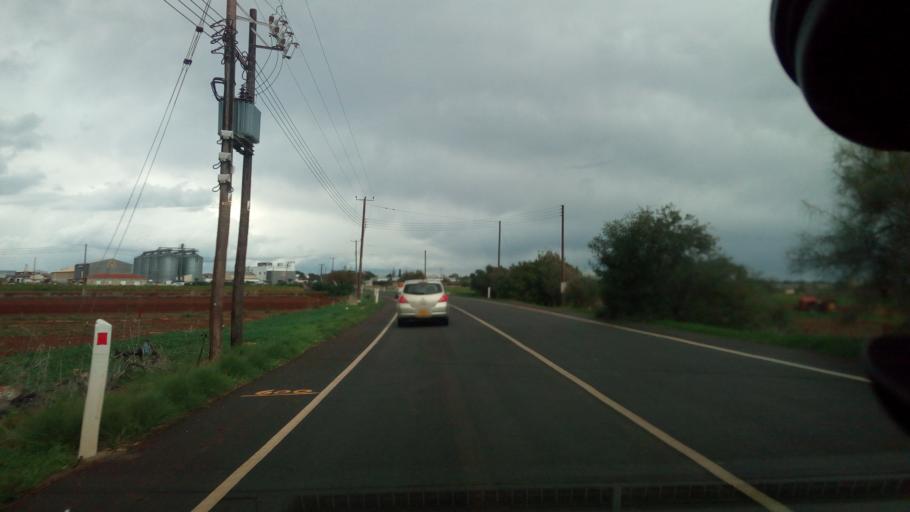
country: CY
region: Ammochostos
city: Liopetri
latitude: 35.0244
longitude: 33.9079
